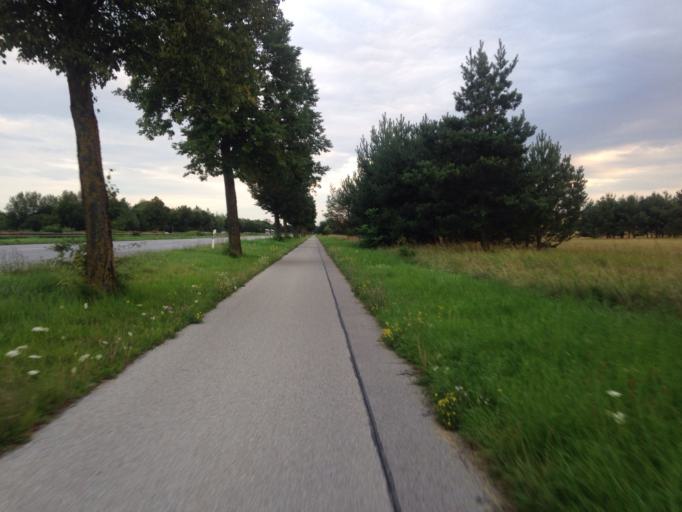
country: DE
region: Bavaria
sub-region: Upper Bavaria
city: Oberschleissheim
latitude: 48.2188
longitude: 11.5875
